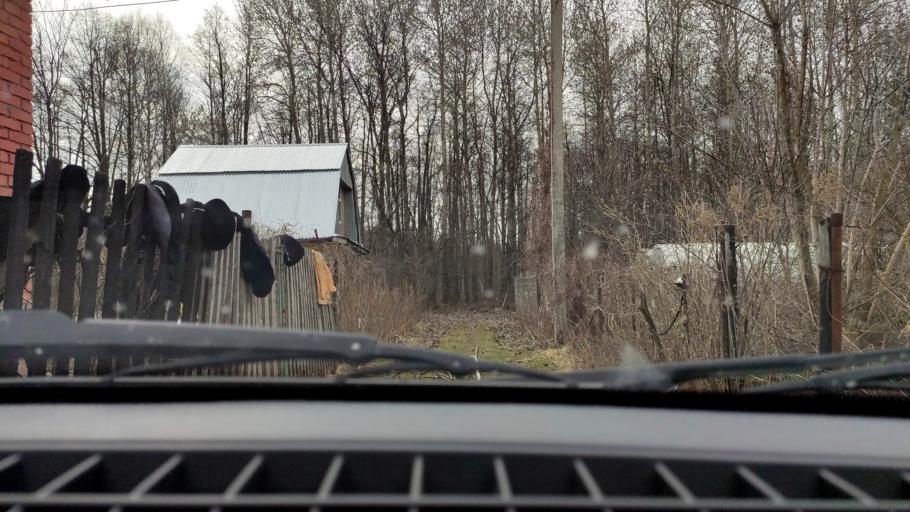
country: RU
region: Bashkortostan
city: Avdon
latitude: 54.6237
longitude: 55.7186
